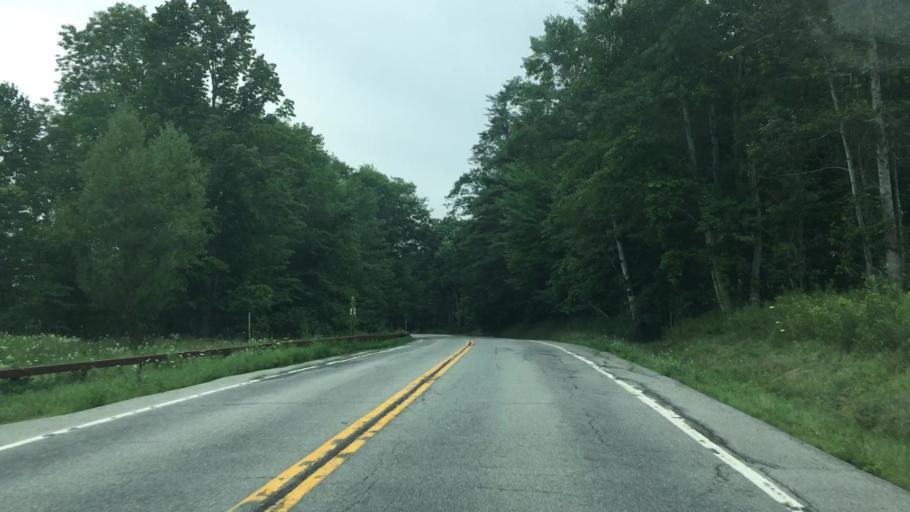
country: US
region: New York
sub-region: Essex County
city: Elizabethtown
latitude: 44.3966
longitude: -73.7088
